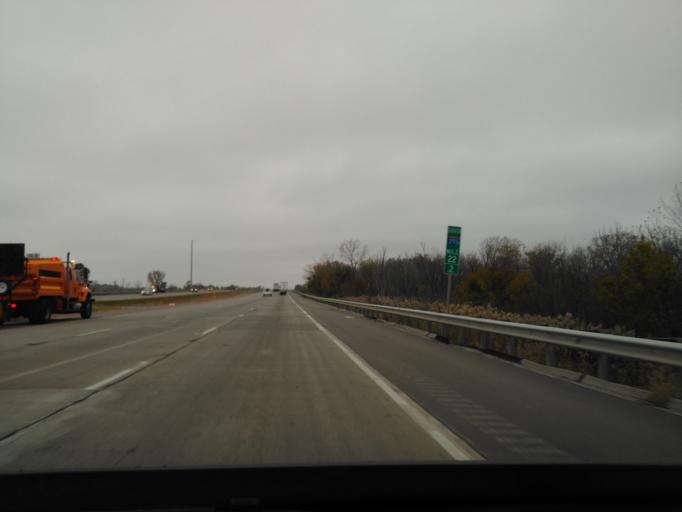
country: US
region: Illinois
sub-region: Saint Clair County
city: Caseyville
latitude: 38.6426
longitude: -90.0492
